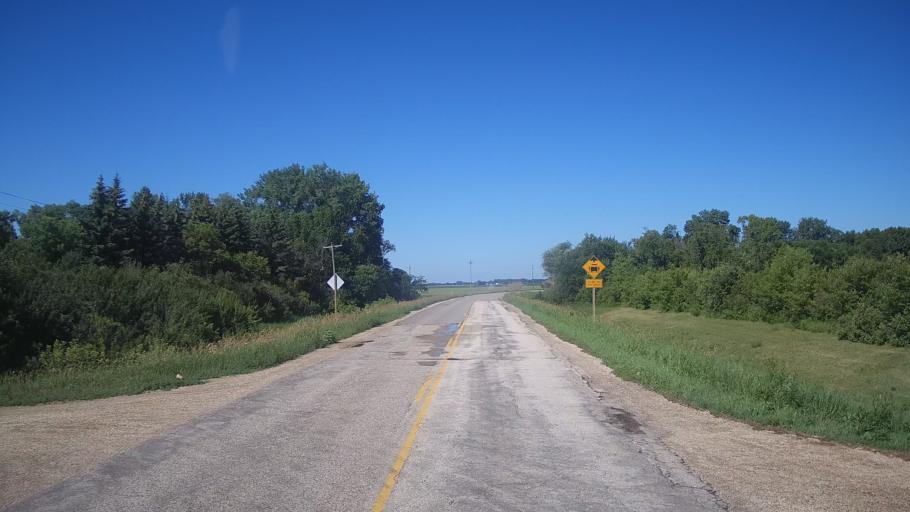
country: CA
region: Manitoba
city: Portage la Prairie
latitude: 50.0443
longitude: -98.0299
